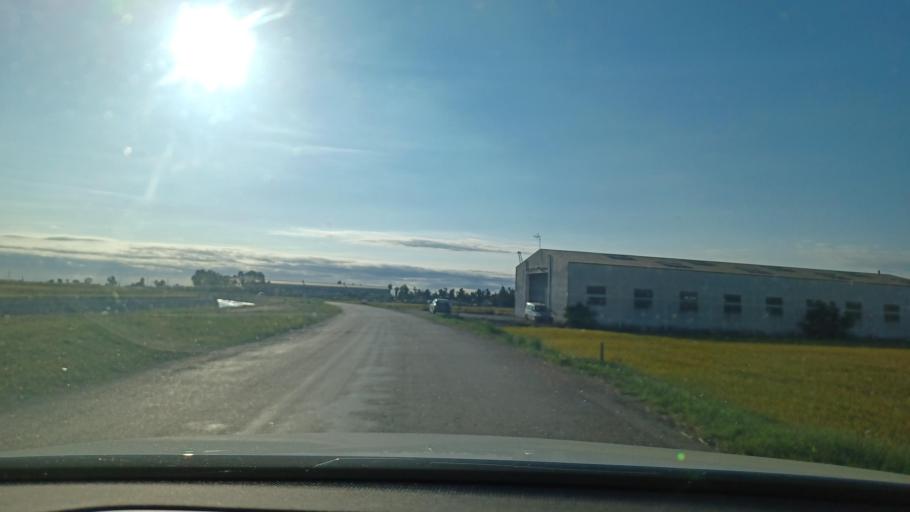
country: ES
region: Catalonia
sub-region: Provincia de Tarragona
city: Amposta
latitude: 40.7020
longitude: 0.5980
